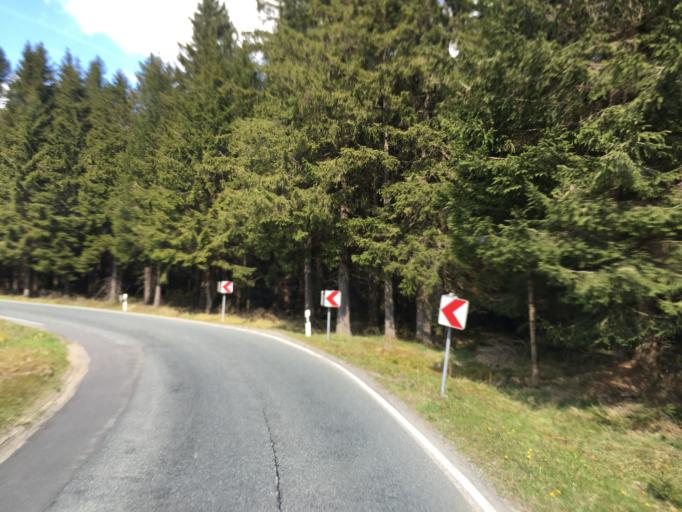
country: DE
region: Saxony-Anhalt
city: Benneckenstein
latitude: 51.7015
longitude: 10.6888
